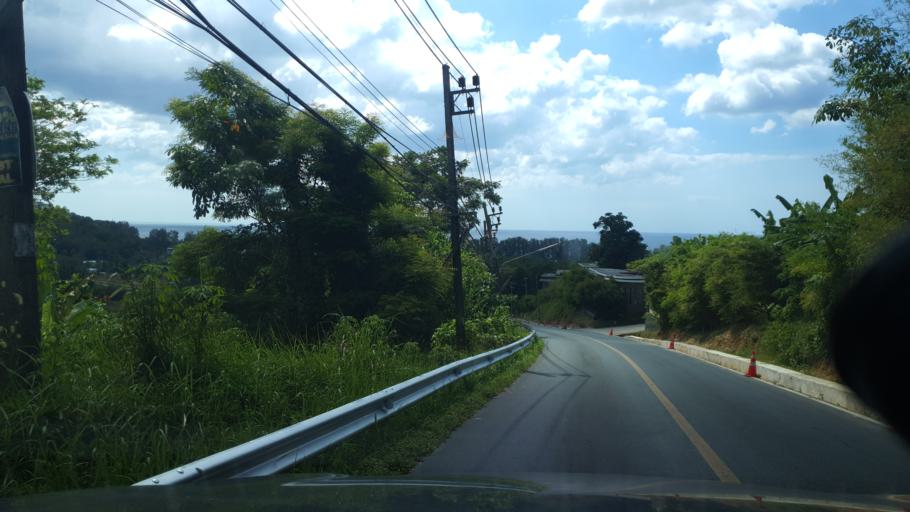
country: TH
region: Phuket
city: Thalang
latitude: 8.0638
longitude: 98.2844
